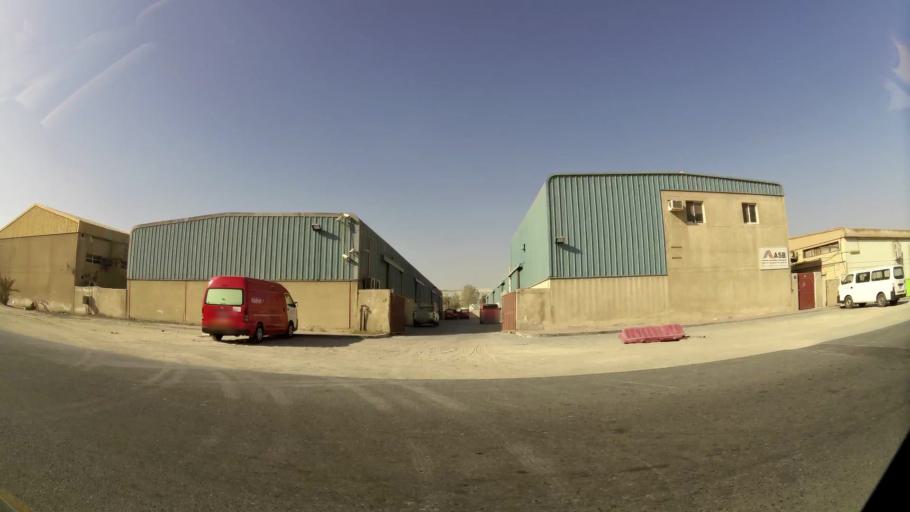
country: AE
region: Dubai
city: Dubai
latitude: 25.1186
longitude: 55.2282
